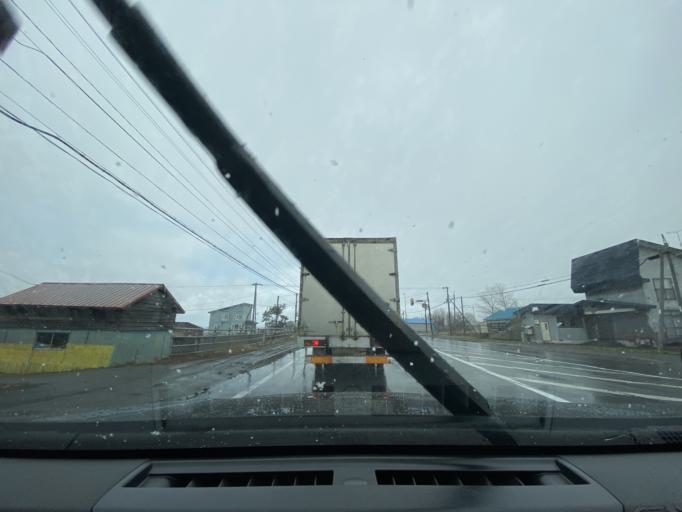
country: JP
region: Hokkaido
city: Takikawa
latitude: 43.6341
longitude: 141.9453
